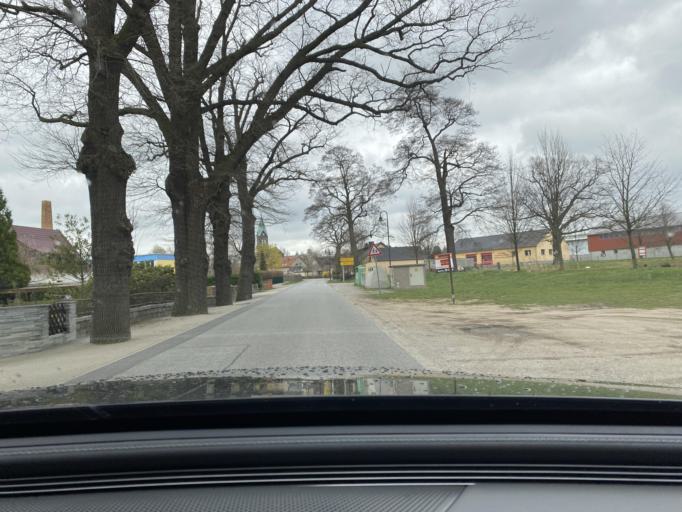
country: DE
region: Saxony
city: Radibor
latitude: 51.2449
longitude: 14.3917
